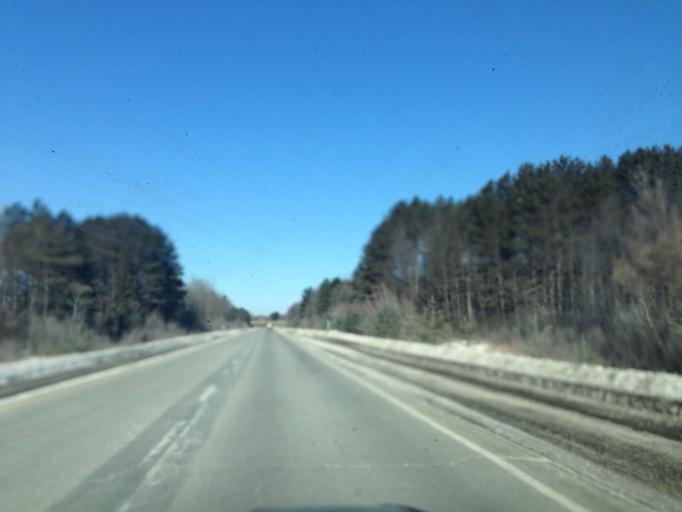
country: CA
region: Ontario
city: Ottawa
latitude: 45.3565
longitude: -75.4693
